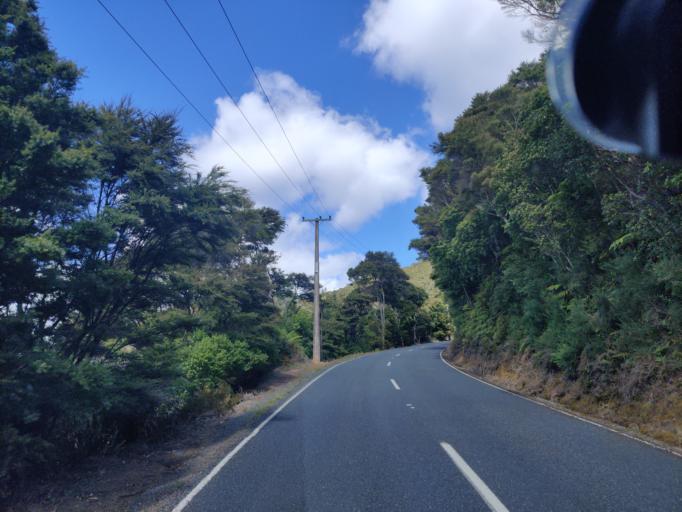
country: NZ
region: Northland
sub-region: Far North District
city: Paihia
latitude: -35.2613
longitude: 174.2472
